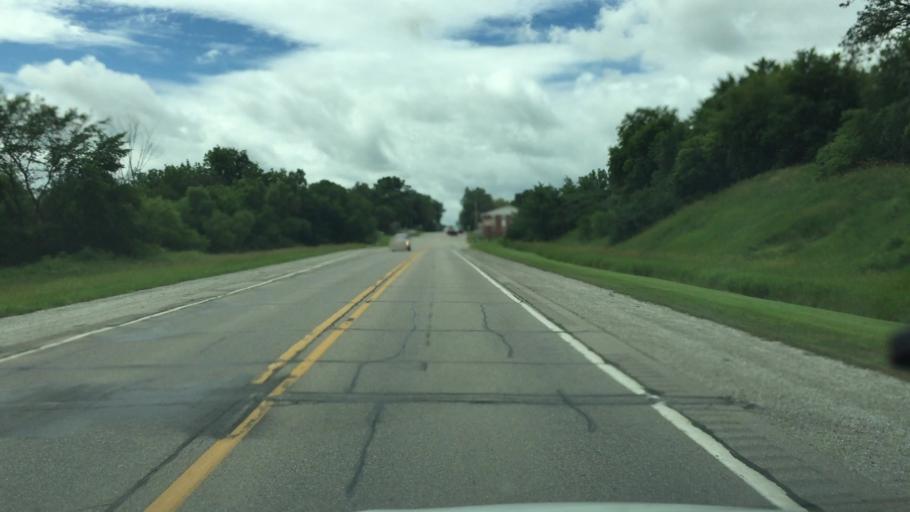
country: US
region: Iowa
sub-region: Jasper County
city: Monroe
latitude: 41.5299
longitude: -93.1019
